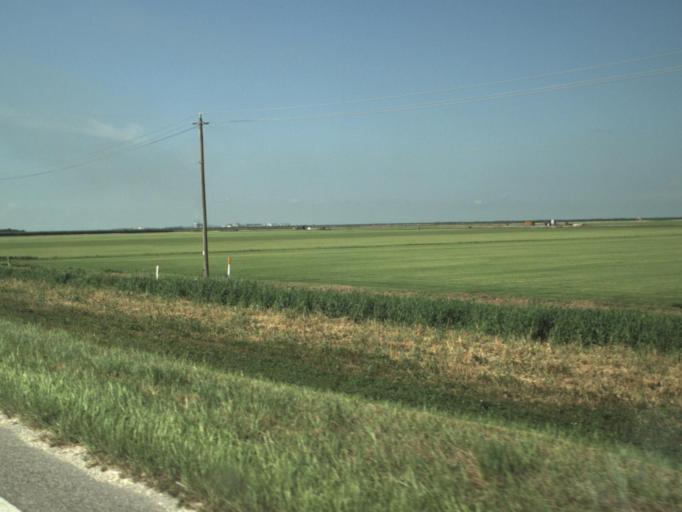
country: US
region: Florida
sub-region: Palm Beach County
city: South Bay
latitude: 26.6382
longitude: -80.7125
